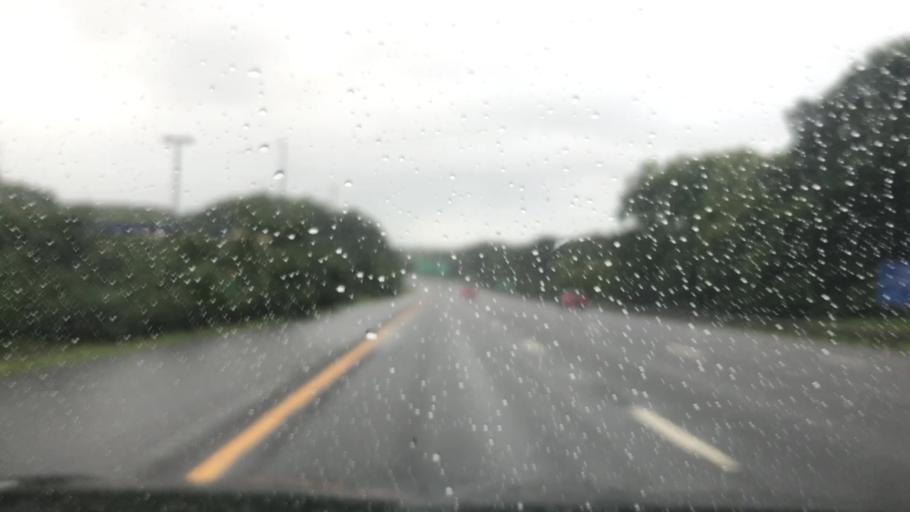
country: US
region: New Jersey
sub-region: Monmouth County
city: Shark River Hills
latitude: 40.1994
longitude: -74.0983
